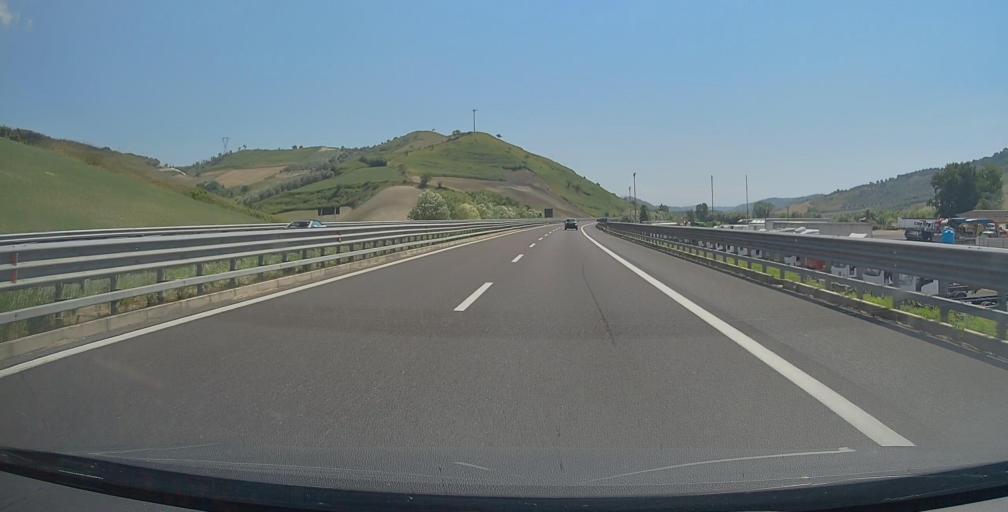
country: IT
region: Calabria
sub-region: Provincia di Vibo-Valentia
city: Francica
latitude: 38.6216
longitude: 16.1595
